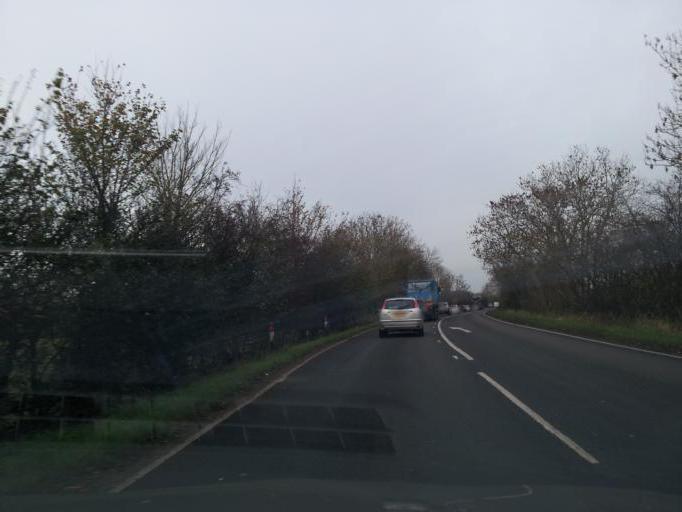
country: GB
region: England
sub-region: Buckinghamshire
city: Aylesbury
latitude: 51.8578
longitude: -0.7667
